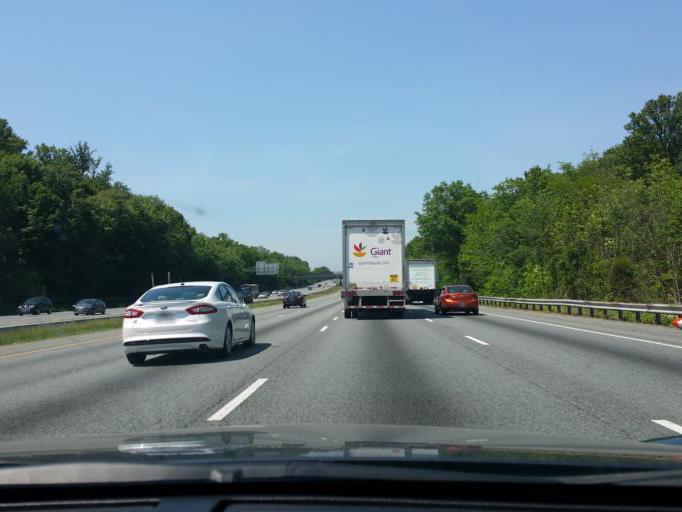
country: US
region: Maryland
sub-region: Howard County
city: West Elkridge
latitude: 39.2143
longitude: -76.7340
